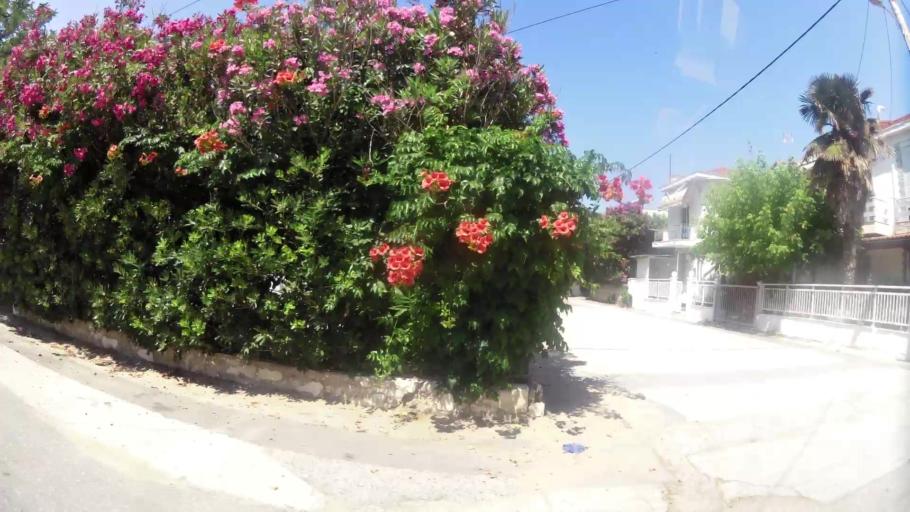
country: GR
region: Central Macedonia
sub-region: Nomos Thessalonikis
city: Agia Triada
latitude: 40.5004
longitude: 22.8791
